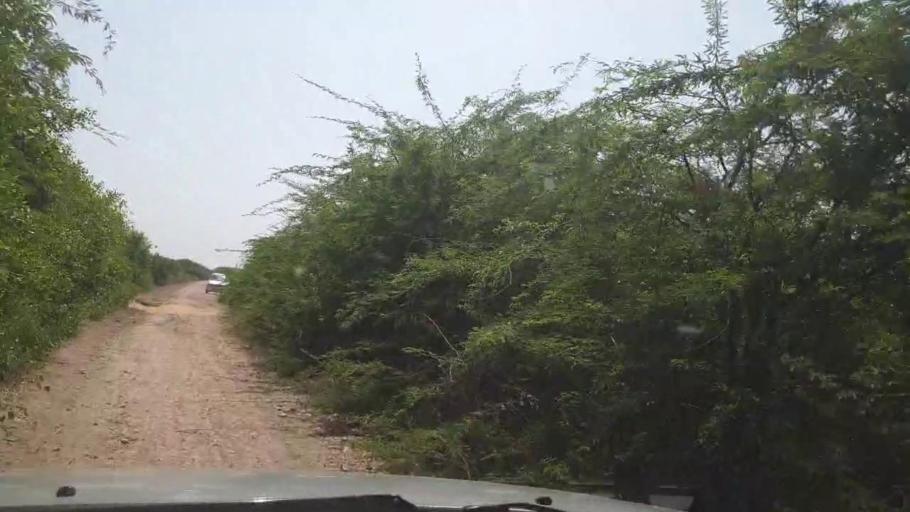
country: PK
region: Sindh
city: Tando Ghulam Ali
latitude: 25.1116
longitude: 68.8101
